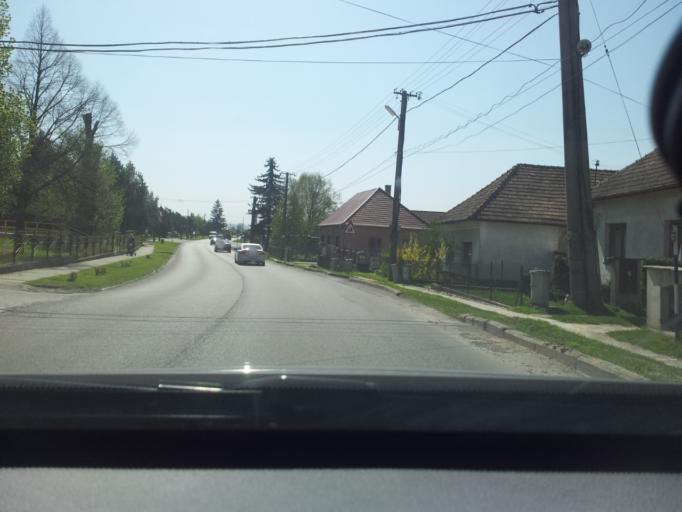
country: SK
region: Nitriansky
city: Banovce nad Bebravou
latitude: 48.6941
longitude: 18.2485
